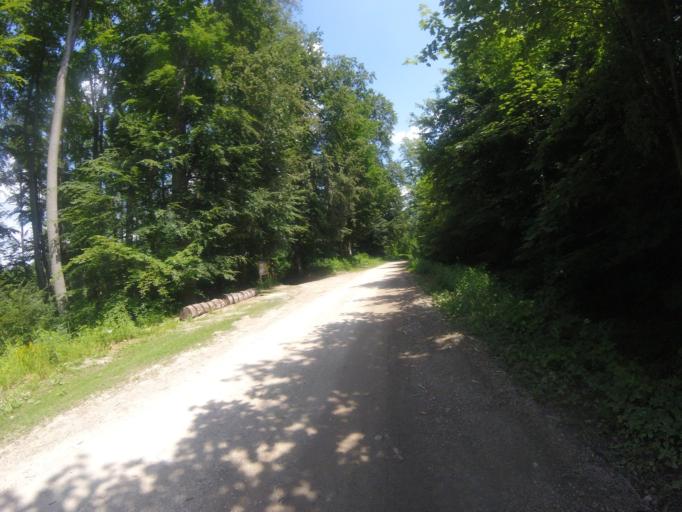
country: HU
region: Veszprem
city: Cseteny
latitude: 47.2680
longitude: 17.9969
